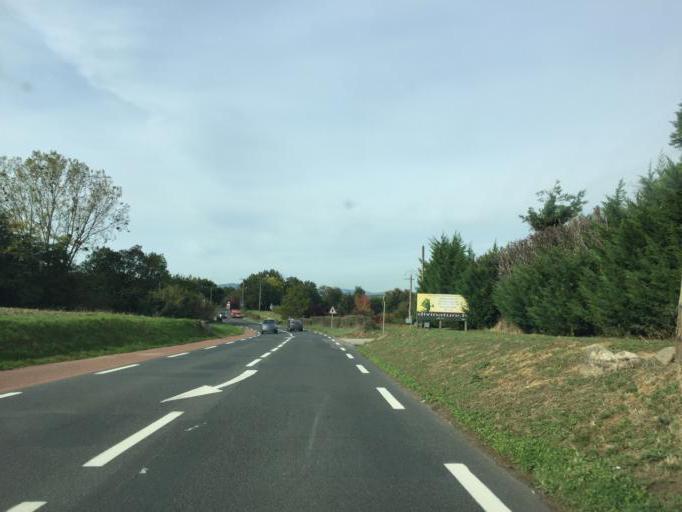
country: FR
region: Rhone-Alpes
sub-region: Departement du Rhone
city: Chasselay
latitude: 45.8723
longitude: 4.7594
